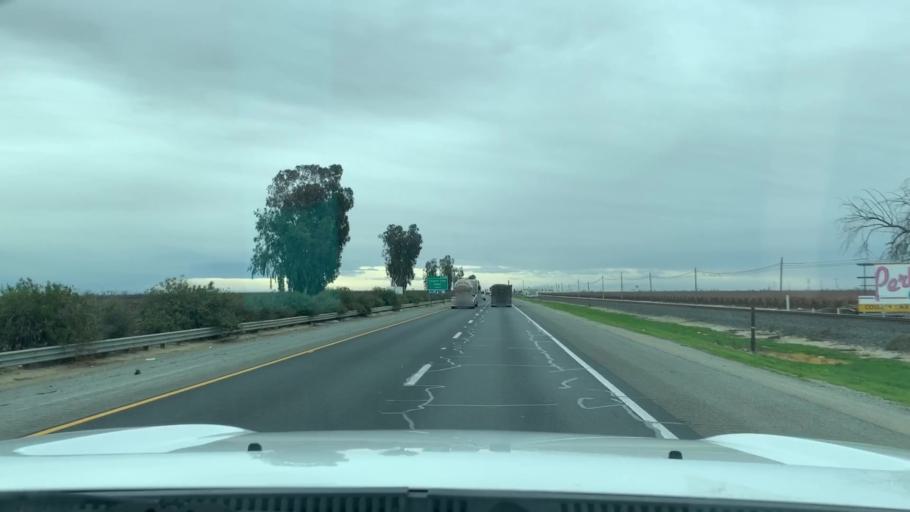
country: US
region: California
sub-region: Kern County
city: Delano
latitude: 35.8127
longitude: -119.2578
